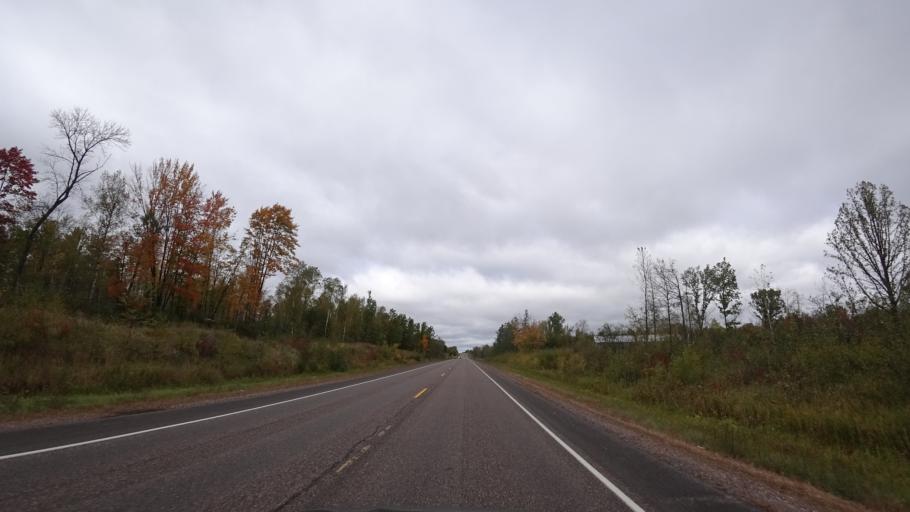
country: US
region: Wisconsin
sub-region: Rusk County
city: Ladysmith
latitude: 45.3897
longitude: -91.1103
